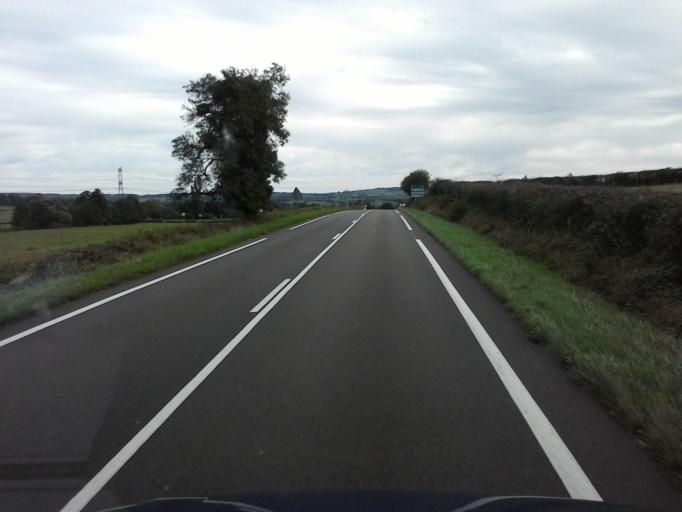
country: FR
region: Bourgogne
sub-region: Departement de Saone-et-Loire
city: Saint-Gengoux-le-National
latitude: 46.5783
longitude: 4.5308
